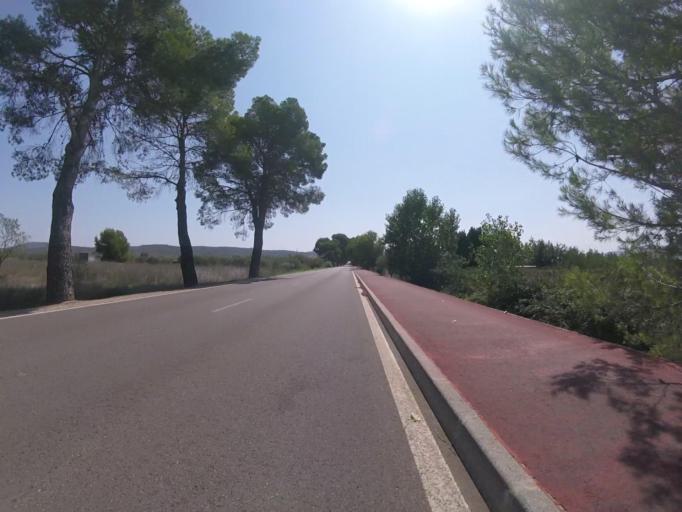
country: ES
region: Valencia
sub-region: Provincia de Castello
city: Cabanes
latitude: 40.1624
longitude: 0.0236
